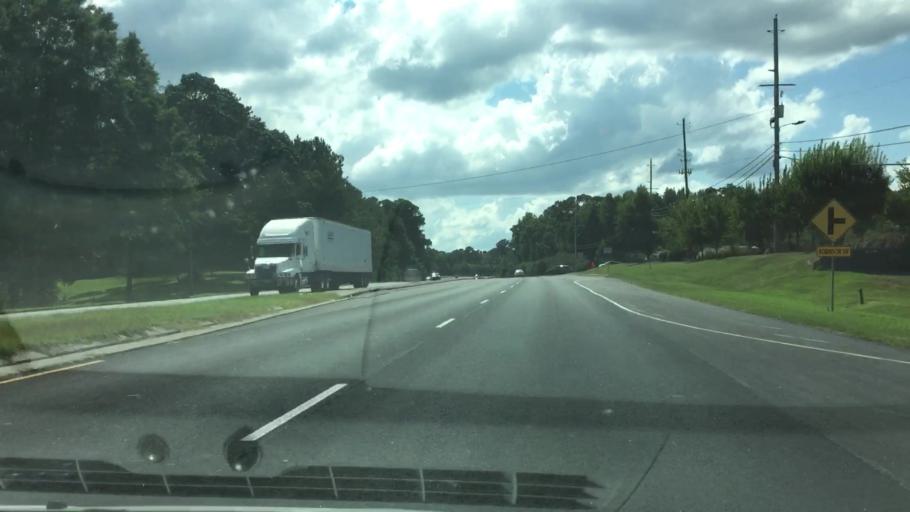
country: US
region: Georgia
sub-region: Fayette County
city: Fayetteville
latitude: 33.4534
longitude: -84.4281
